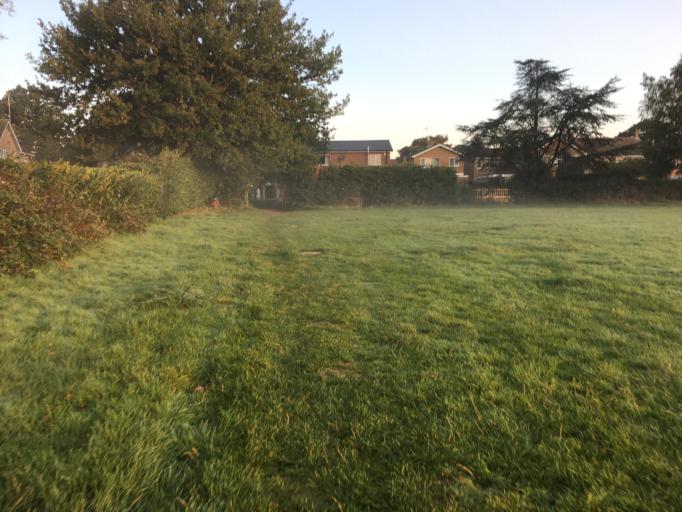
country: GB
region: England
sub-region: Warwickshire
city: Rugby
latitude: 52.3567
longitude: -1.2651
